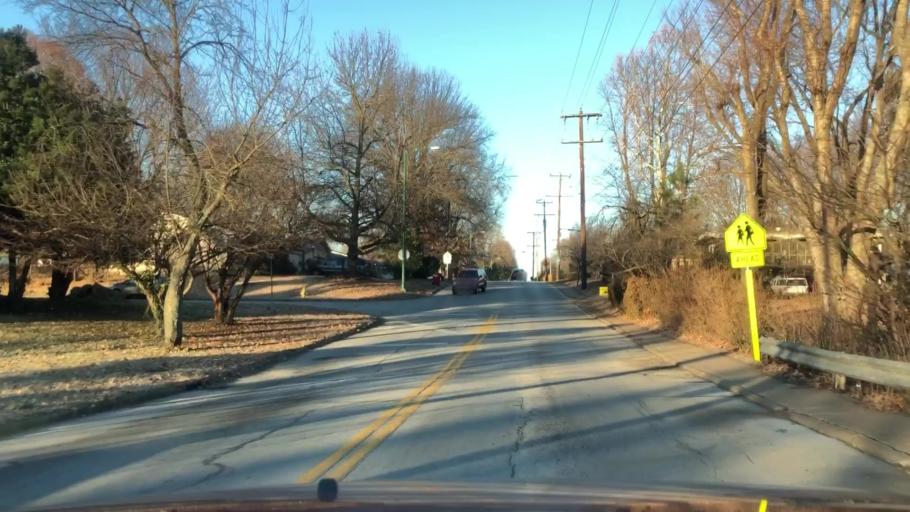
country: US
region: Missouri
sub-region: Greene County
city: Springfield
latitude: 37.1736
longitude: -93.2443
